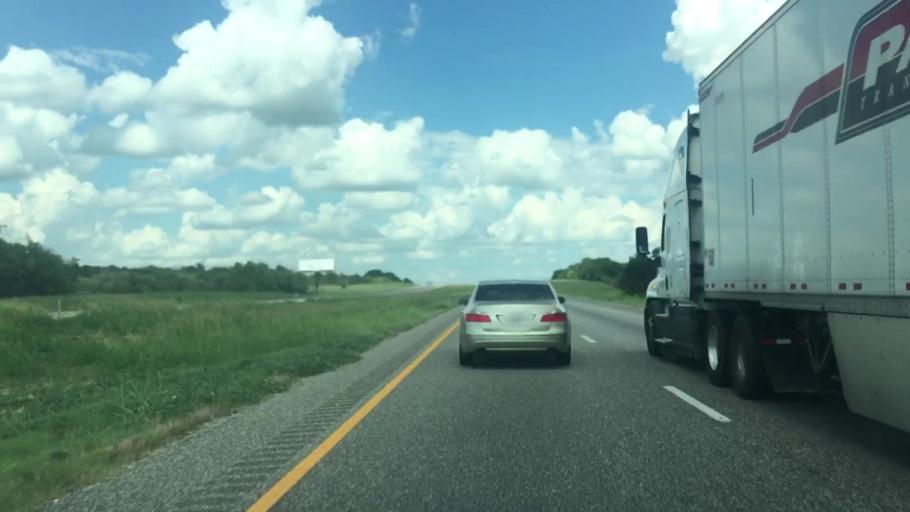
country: US
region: Texas
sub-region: Ellis County
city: Plum Grove
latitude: 32.0885
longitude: -97.0352
